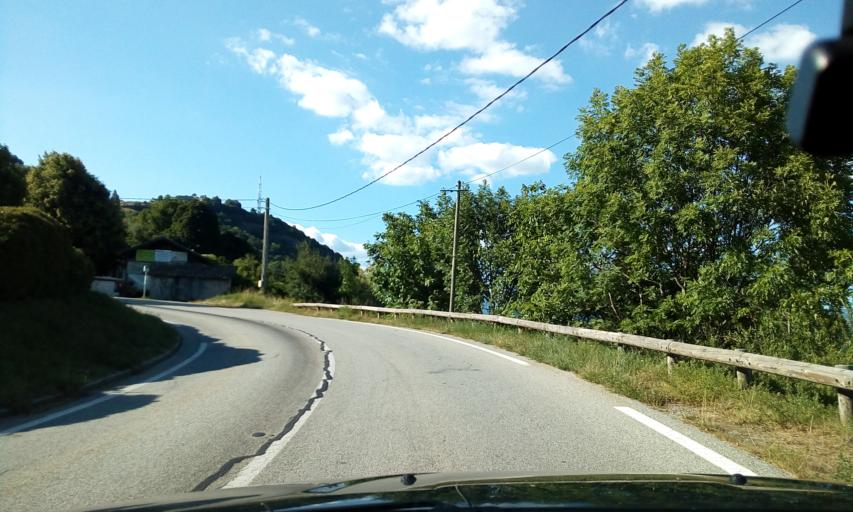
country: FR
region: Rhone-Alpes
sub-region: Departement de l'Isere
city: Seyssins
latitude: 45.1645
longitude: 5.6717
